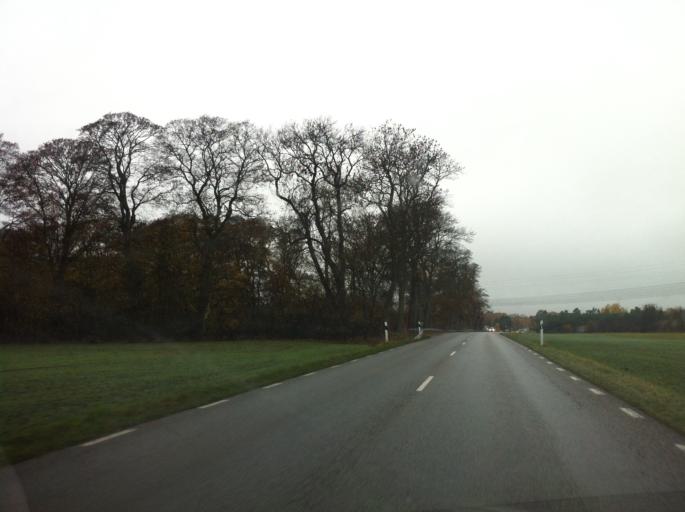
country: SE
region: Skane
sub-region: Kavlinge Kommun
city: Kaevlinge
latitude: 55.8063
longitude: 13.0740
